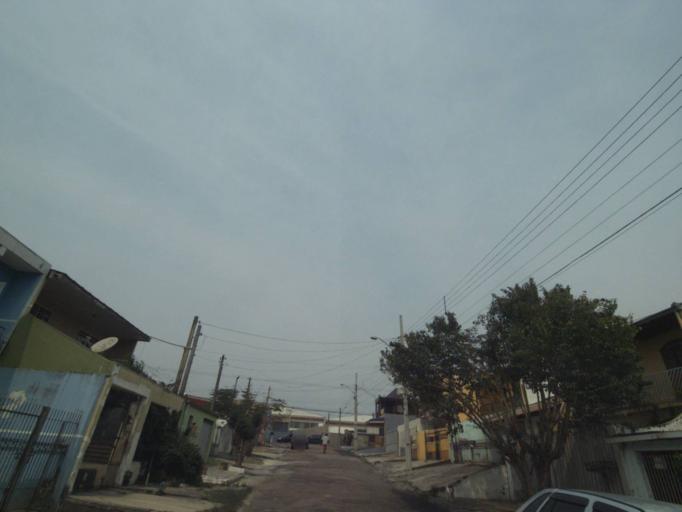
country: BR
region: Parana
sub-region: Sao Jose Dos Pinhais
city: Sao Jose dos Pinhais
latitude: -25.5210
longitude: -49.2888
